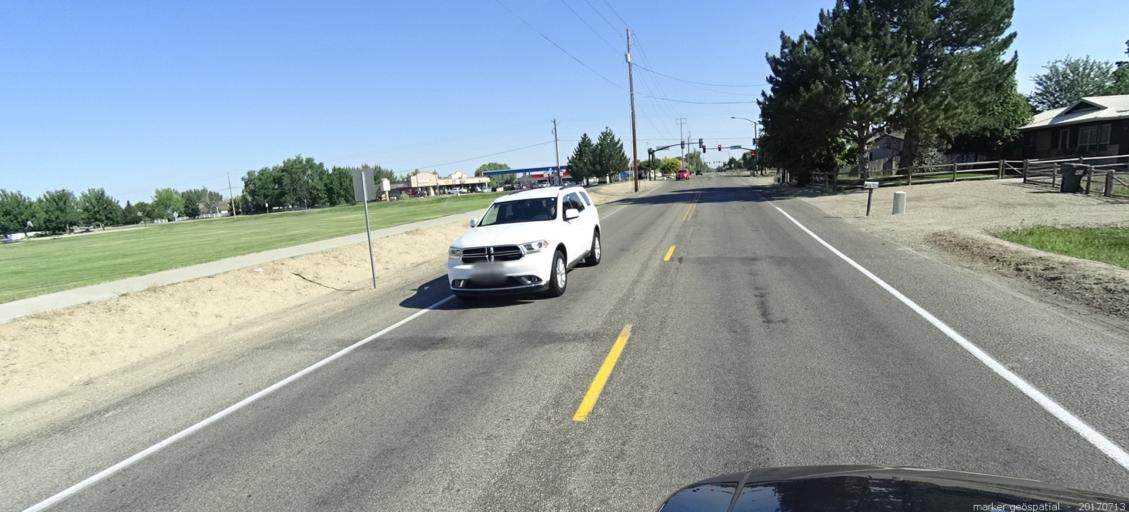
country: US
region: Idaho
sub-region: Ada County
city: Kuna
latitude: 43.5019
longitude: -116.4137
